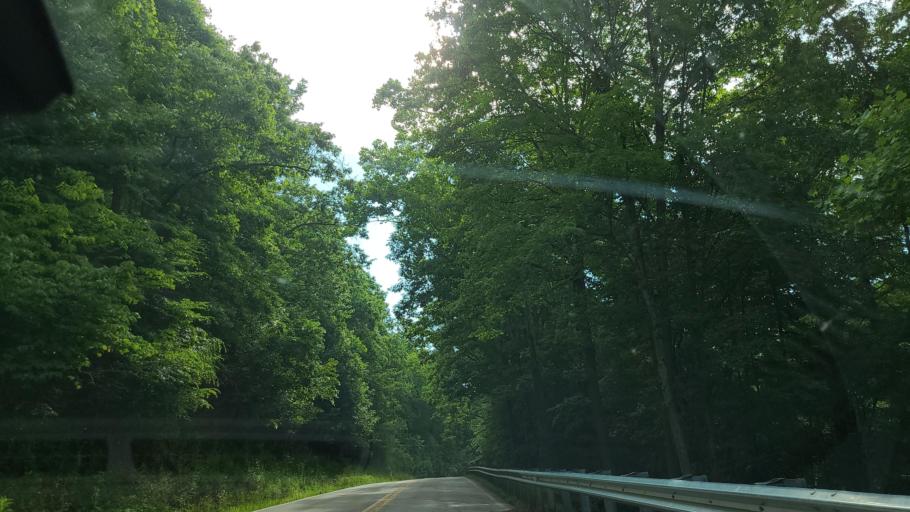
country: US
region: Kentucky
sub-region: Knox County
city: Barbourville
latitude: 36.6819
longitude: -83.9227
